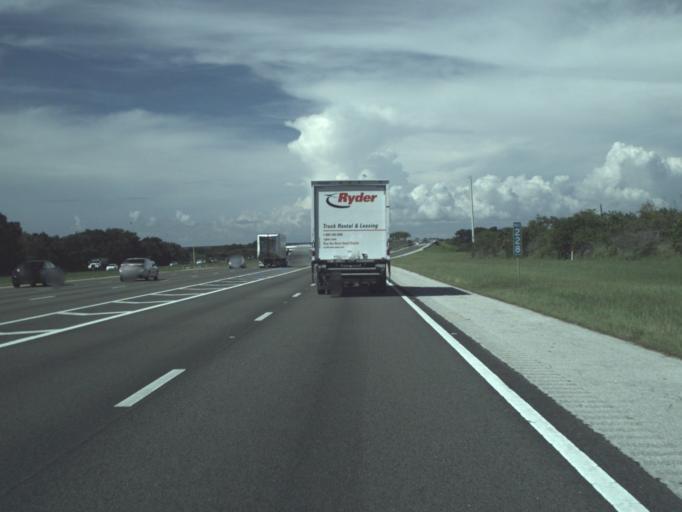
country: US
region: Florida
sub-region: Manatee County
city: Ellenton
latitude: 27.5752
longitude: -82.5143
